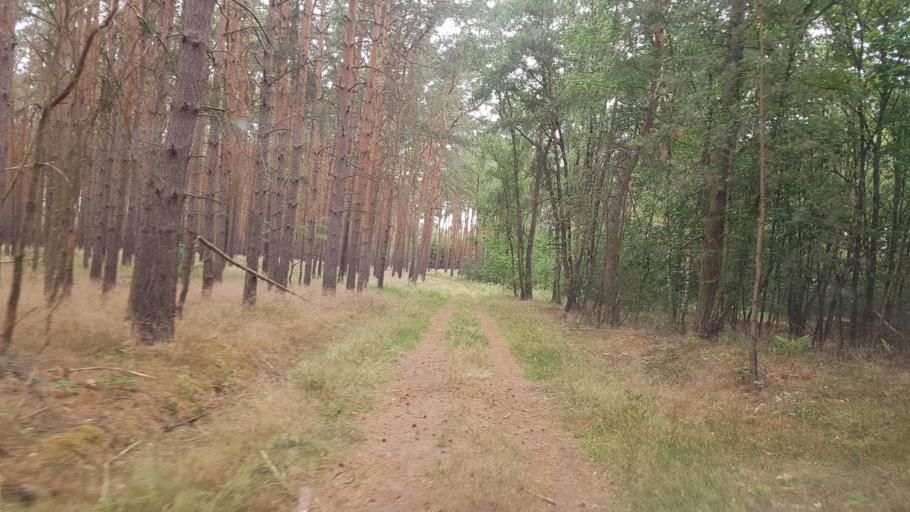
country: DE
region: Brandenburg
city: Treuenbrietzen
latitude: 52.0351
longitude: 12.8406
